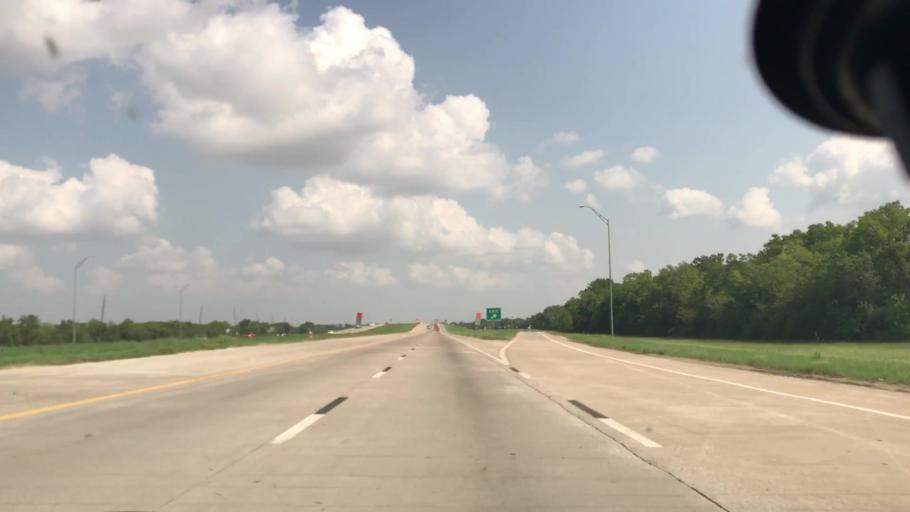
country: US
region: Texas
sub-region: Brazoria County
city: Iowa Colony
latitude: 29.5050
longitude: -95.3880
